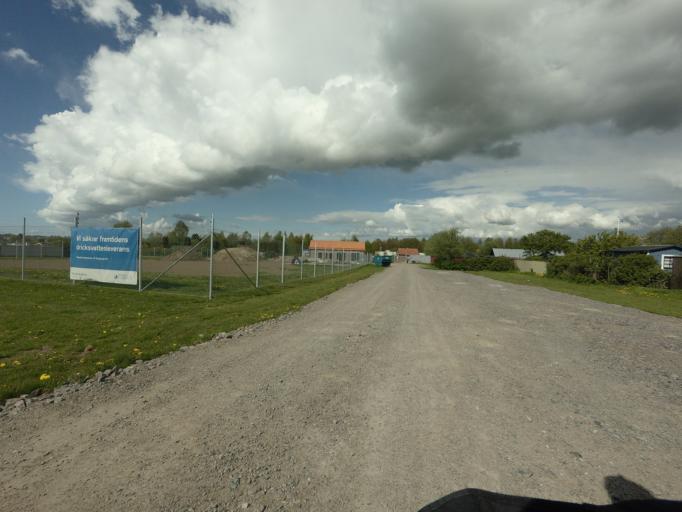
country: SE
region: Skane
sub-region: Landskrona
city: Landskrona
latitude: 55.8946
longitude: 12.8491
